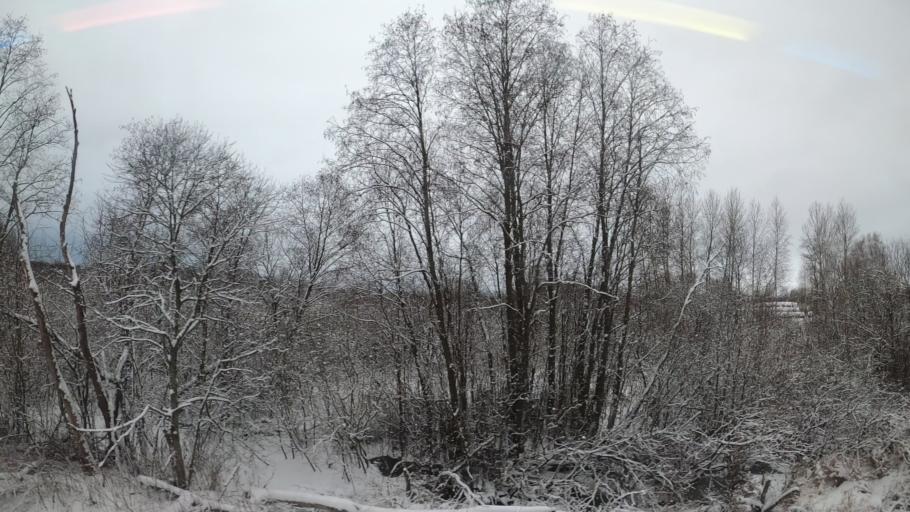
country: RU
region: Jaroslavl
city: Pereslavl'-Zalesskiy
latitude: 56.7202
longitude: 38.9072
